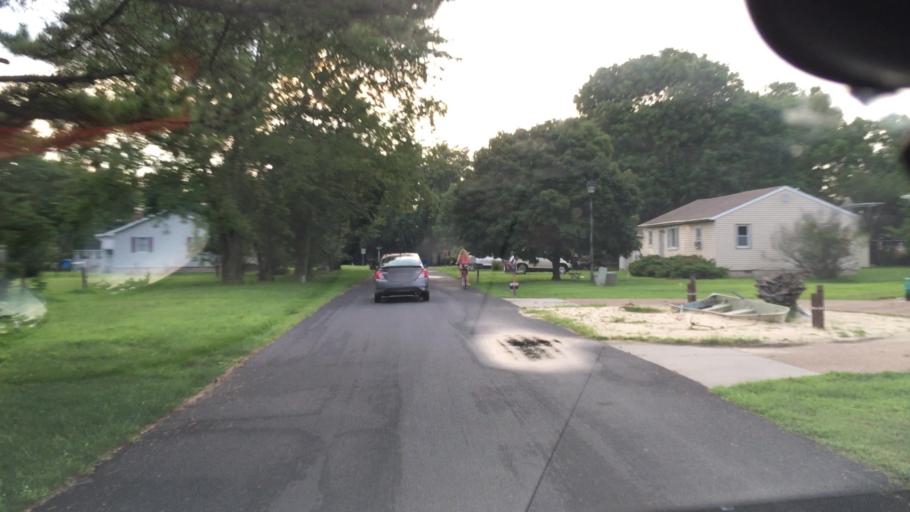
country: US
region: Delaware
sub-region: Sussex County
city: Ocean View
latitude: 38.5396
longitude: -75.0912
